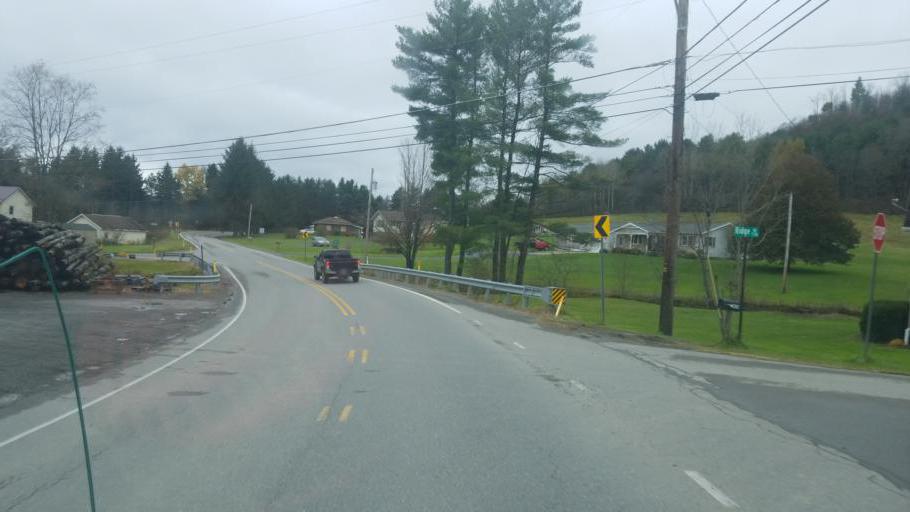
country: US
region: Pennsylvania
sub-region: Elk County
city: Ridgway
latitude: 41.3197
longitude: -78.6407
